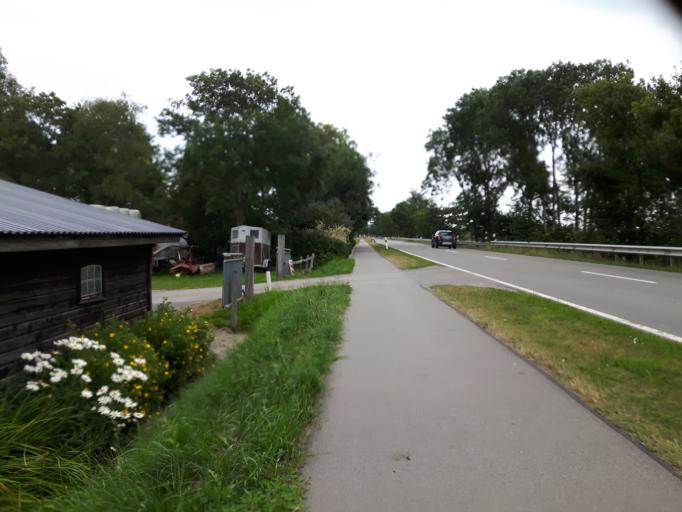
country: DE
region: Lower Saxony
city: Varel
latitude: 53.3880
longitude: 8.2452
